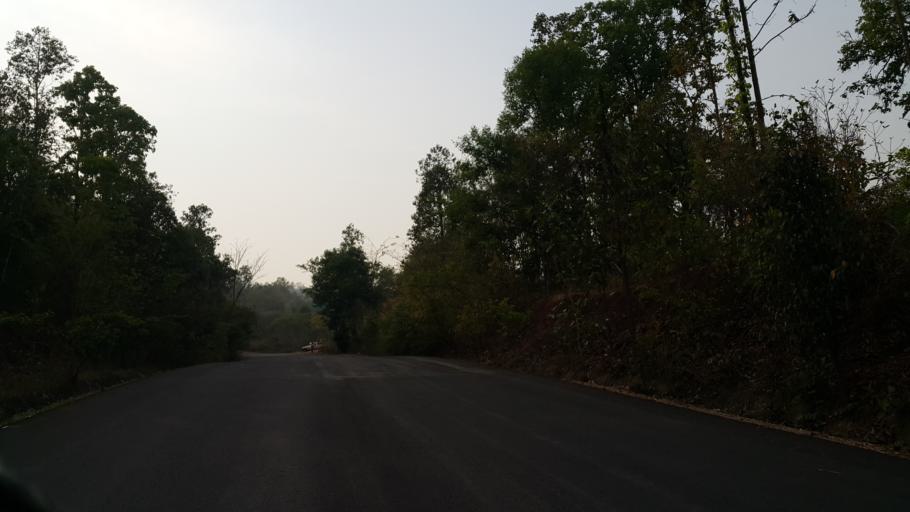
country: TH
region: Chiang Mai
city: Mae On
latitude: 18.7514
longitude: 99.3006
